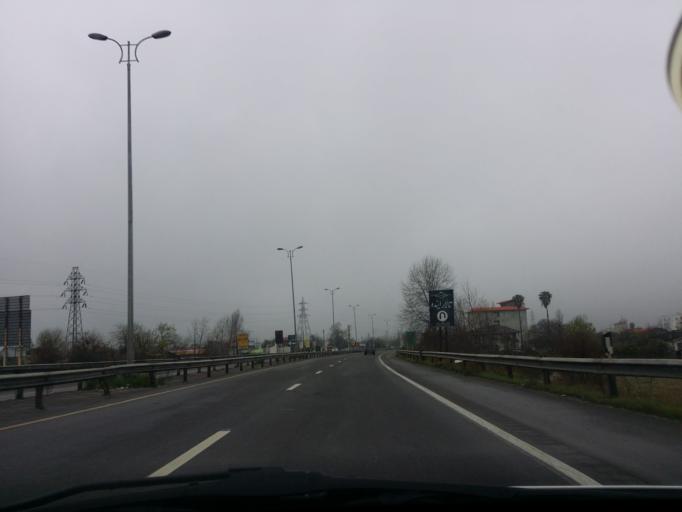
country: IR
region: Mazandaran
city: Tonekabon
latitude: 36.8107
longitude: 50.8589
